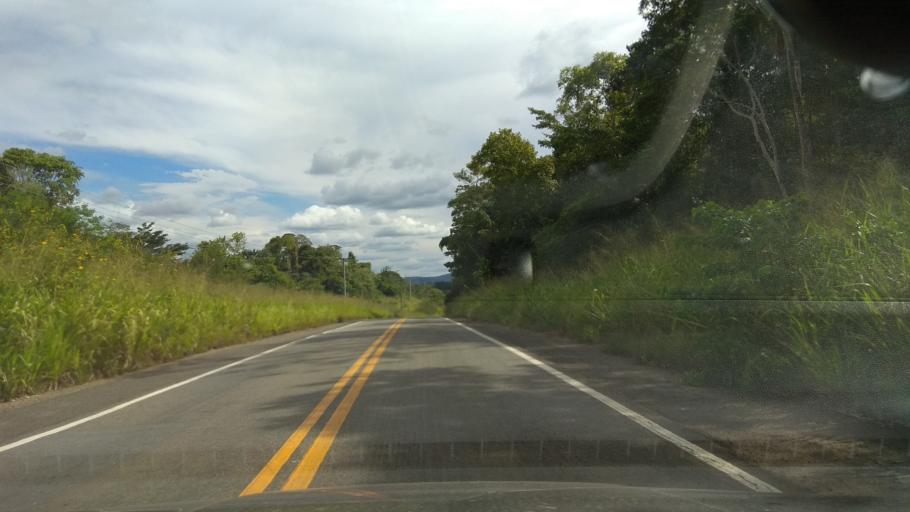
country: BR
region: Bahia
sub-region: Ubata
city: Ubata
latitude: -14.2299
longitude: -39.4510
